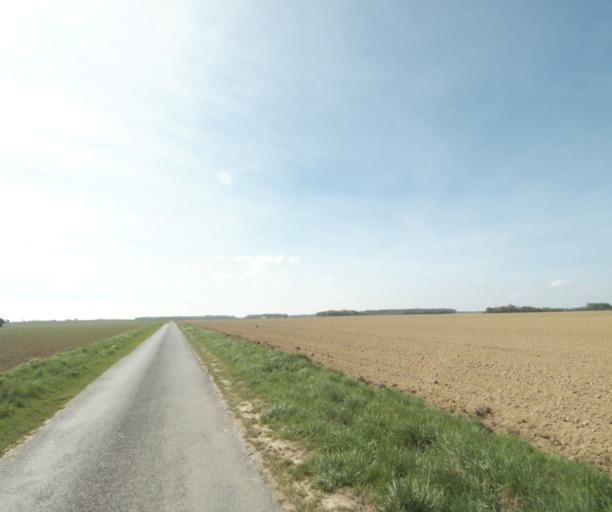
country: FR
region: Ile-de-France
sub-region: Departement de Seine-et-Marne
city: Nangis
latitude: 48.5429
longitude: 3.0367
